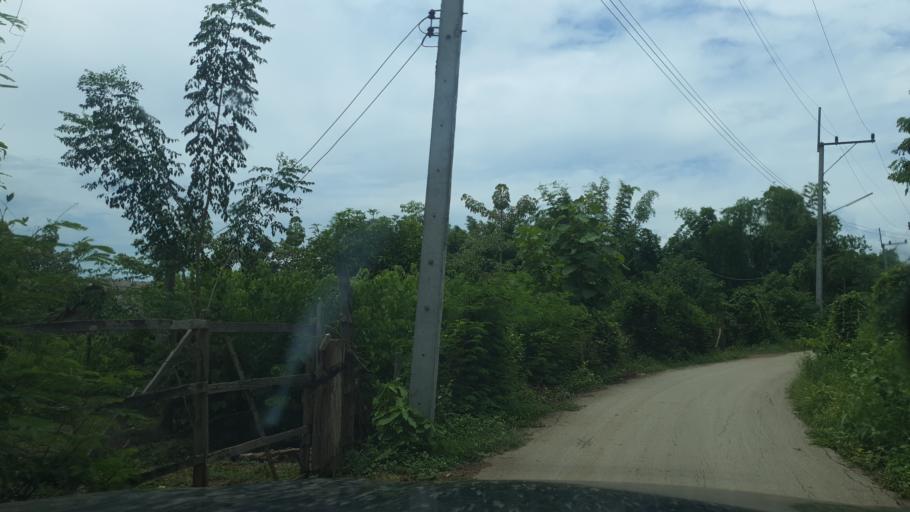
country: TH
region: Lampang
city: Ko Kha
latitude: 18.1267
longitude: 99.3483
